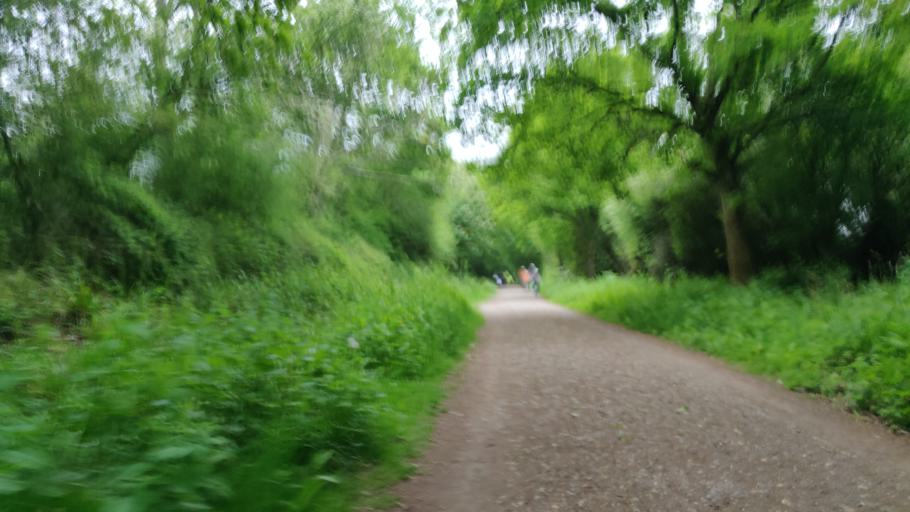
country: GB
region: England
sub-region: West Sussex
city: Southwater
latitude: 51.0136
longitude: -0.3352
